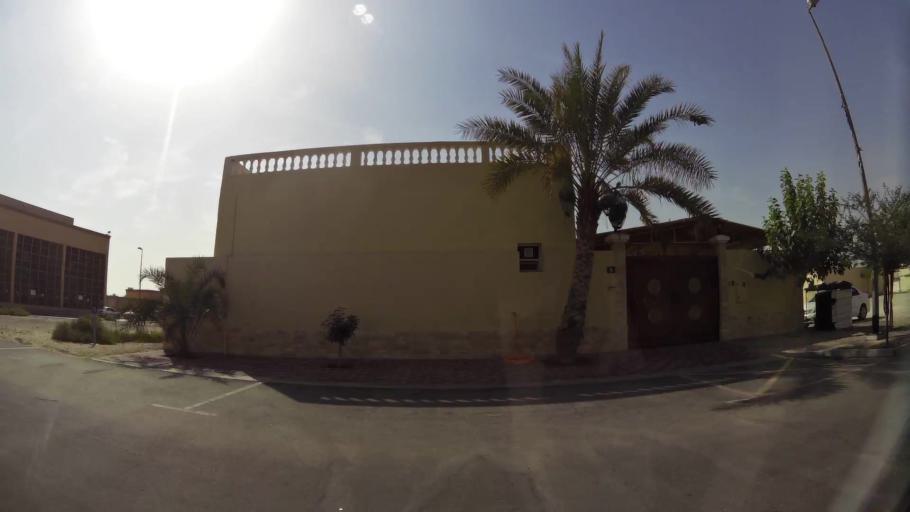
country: AE
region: Ash Shariqah
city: Sharjah
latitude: 25.2604
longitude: 55.3950
